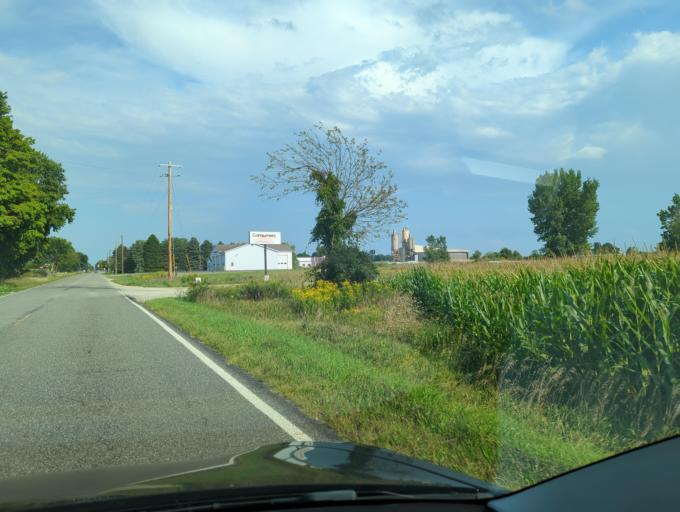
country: US
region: Michigan
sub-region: Ionia County
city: Ionia
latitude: 42.9296
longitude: -85.0805
